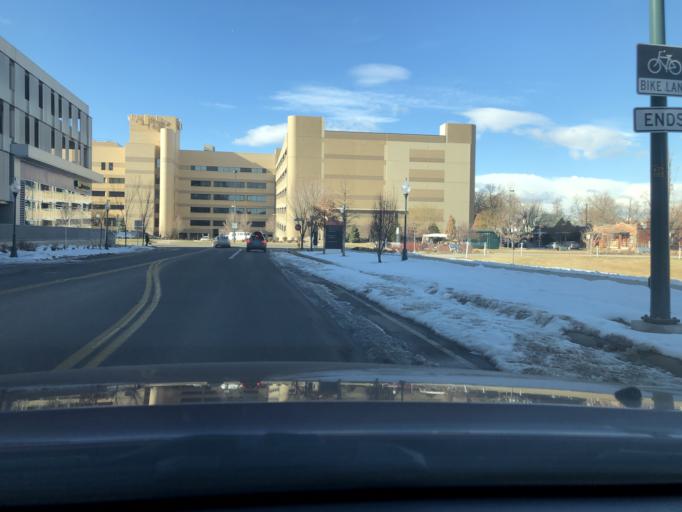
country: US
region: Colorado
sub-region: Denver County
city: Denver
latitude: 39.7470
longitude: -104.9724
